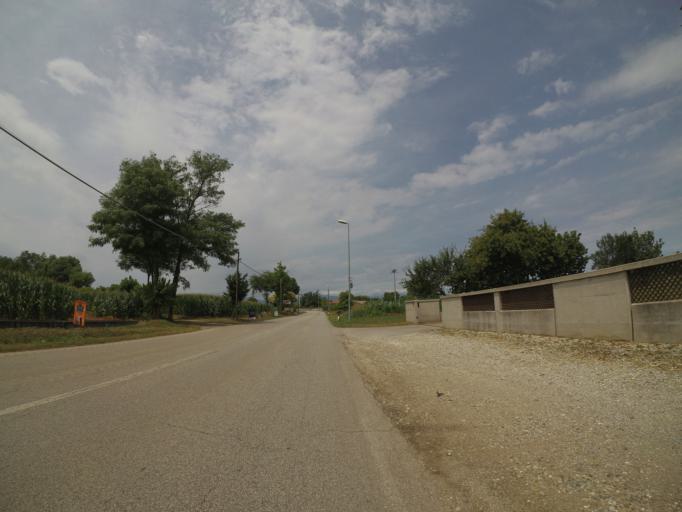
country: IT
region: Friuli Venezia Giulia
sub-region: Provincia di Udine
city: Sedegliano
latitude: 46.0028
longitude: 12.9935
